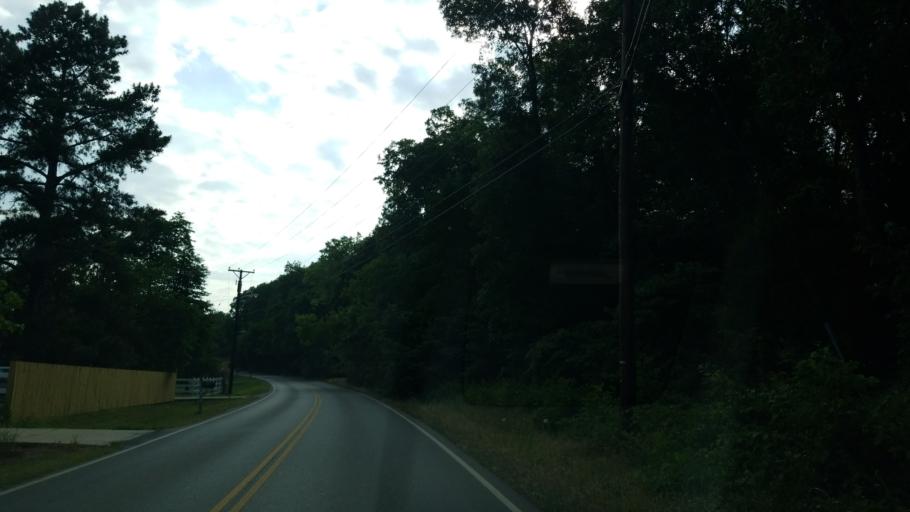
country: US
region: Tennessee
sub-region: Rutherford County
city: La Vergne
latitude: 36.0408
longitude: -86.5986
